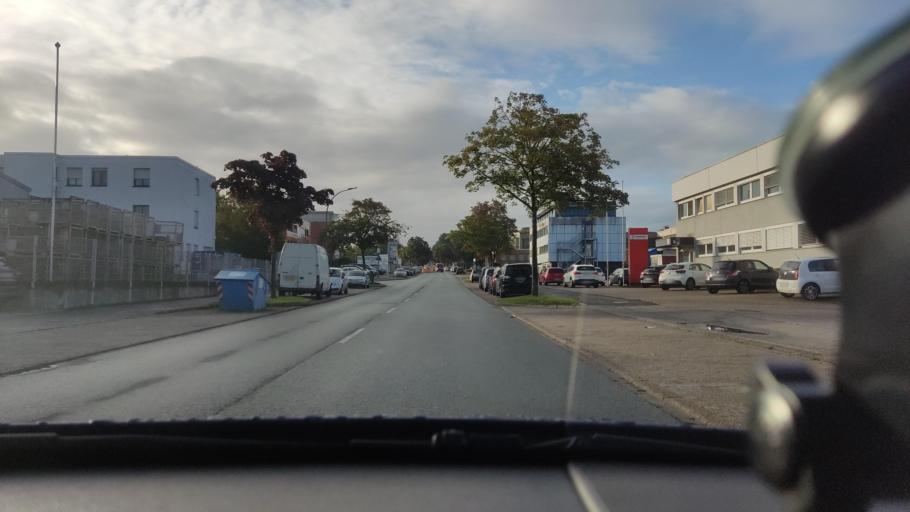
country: DE
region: North Rhine-Westphalia
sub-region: Regierungsbezirk Arnsberg
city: Dortmund
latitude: 51.5065
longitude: 7.3926
